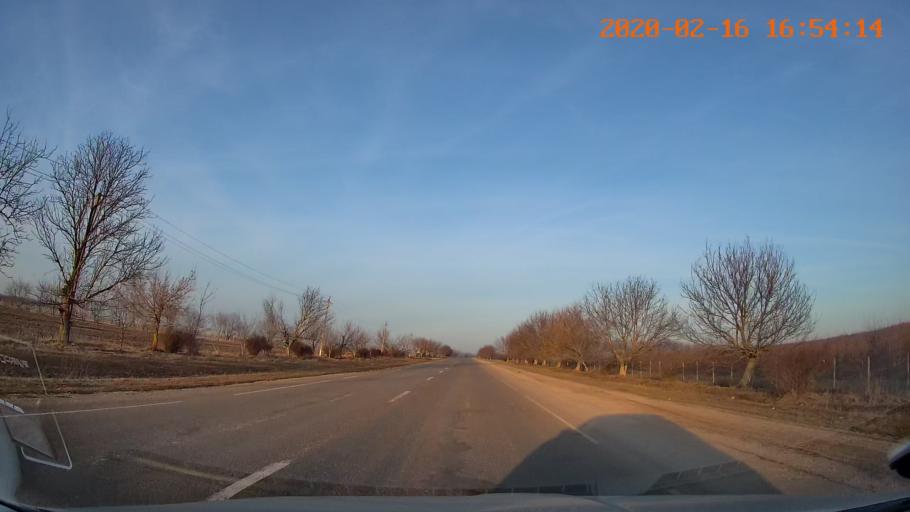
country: MD
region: Briceni
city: Briceni
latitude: 48.3187
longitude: 27.0030
